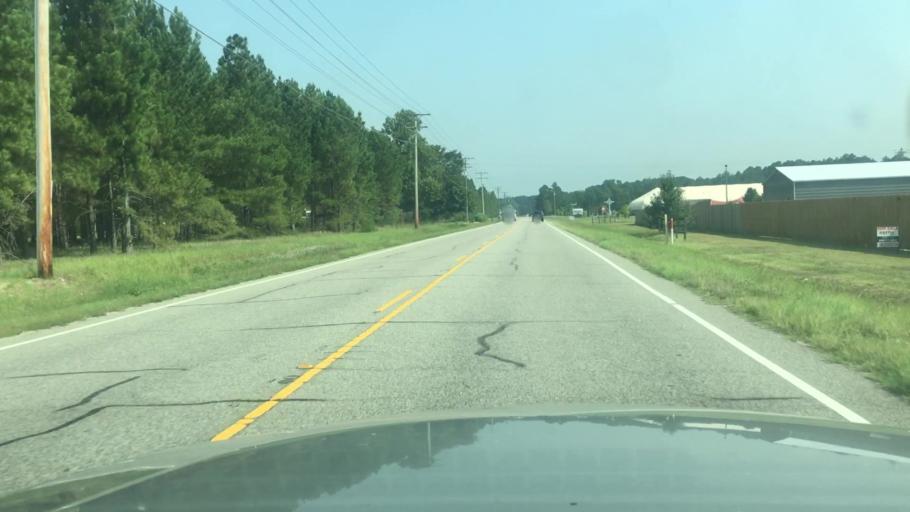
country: US
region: North Carolina
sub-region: Cumberland County
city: Hope Mills
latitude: 34.9035
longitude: -78.9019
